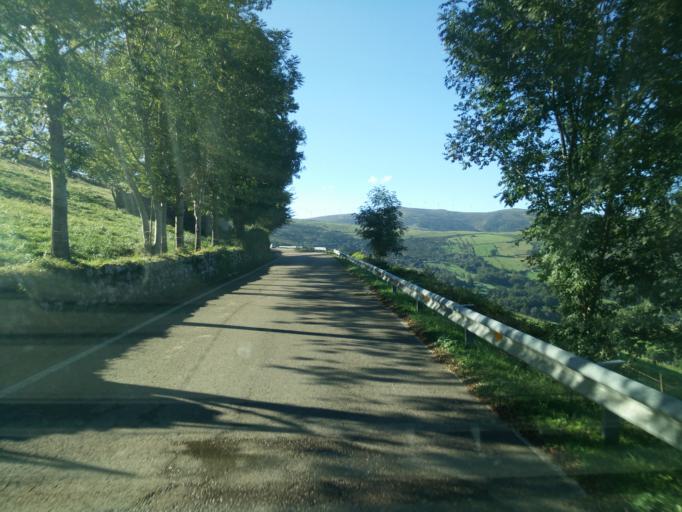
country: ES
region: Cantabria
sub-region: Provincia de Cantabria
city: San Pedro del Romeral
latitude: 43.0995
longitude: -3.8194
